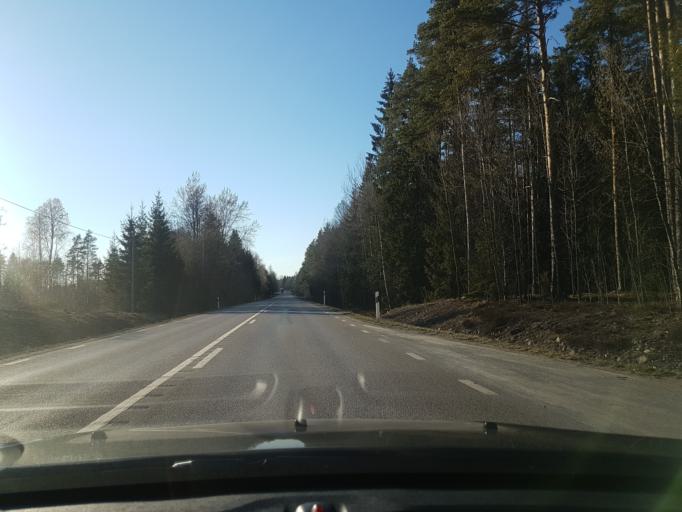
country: SE
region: Uppsala
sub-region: Heby Kommun
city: Morgongava
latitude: 59.9000
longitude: 17.0870
